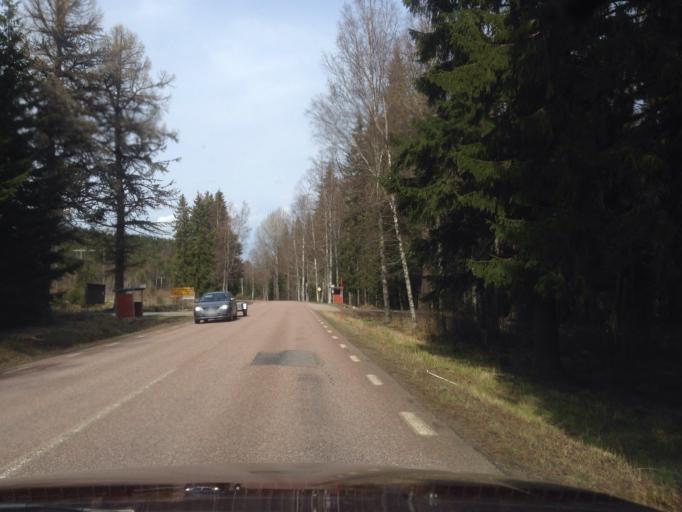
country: SE
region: Dalarna
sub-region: Ludvika Kommun
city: Grangesberg
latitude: 60.1232
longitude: 15.0095
